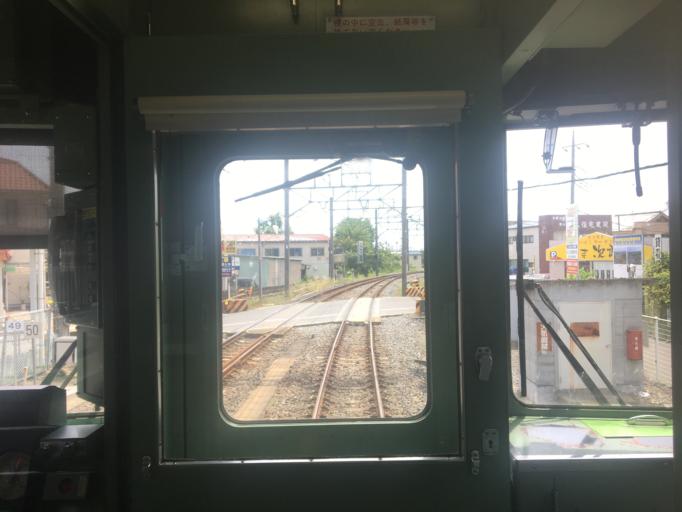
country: JP
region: Saitama
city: Morohongo
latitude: 35.9374
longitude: 139.3469
